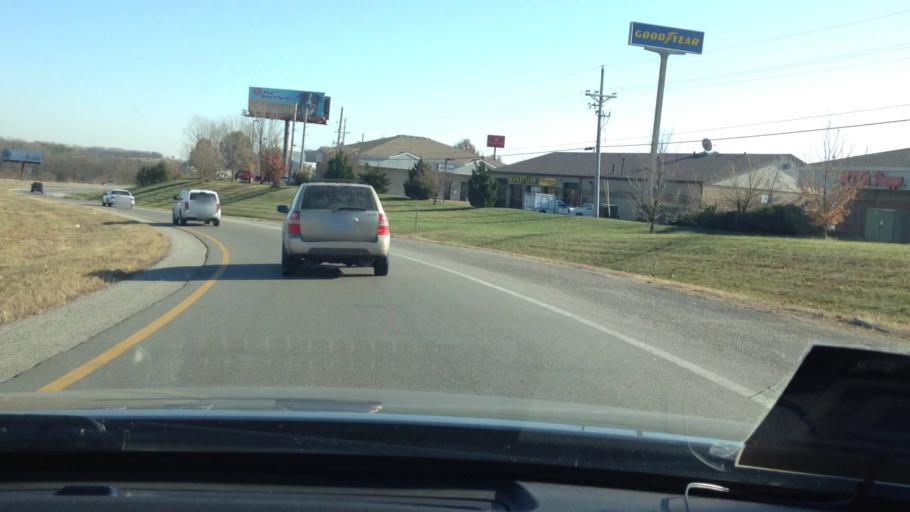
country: US
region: Missouri
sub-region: Platte County
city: Platte City
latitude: 39.3527
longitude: -94.7629
